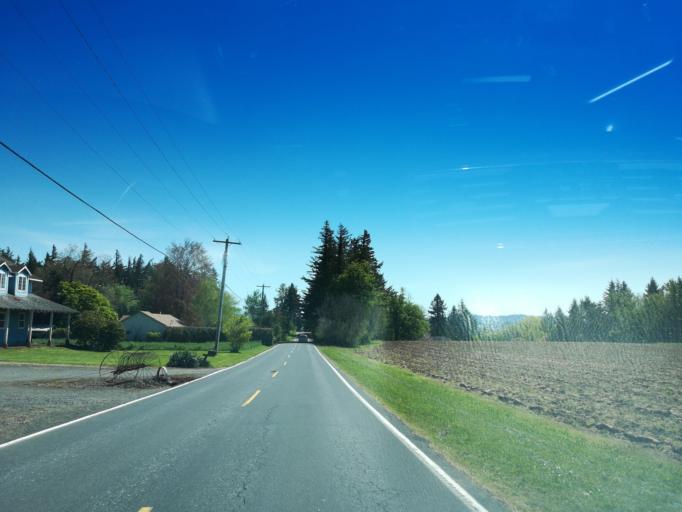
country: US
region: Oregon
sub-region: Multnomah County
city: Troutdale
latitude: 45.5254
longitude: -122.3523
